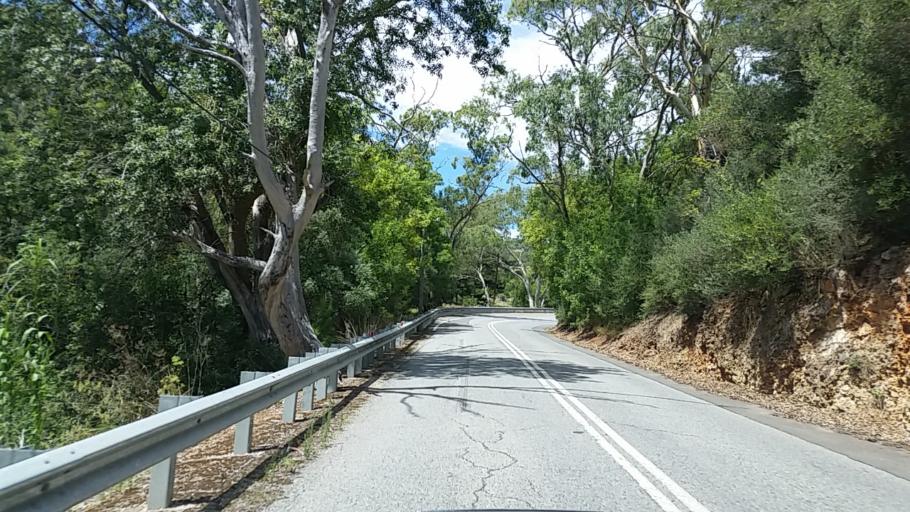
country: AU
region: South Australia
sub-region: Campbelltown
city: Athelstone
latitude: -34.8659
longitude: 138.7507
